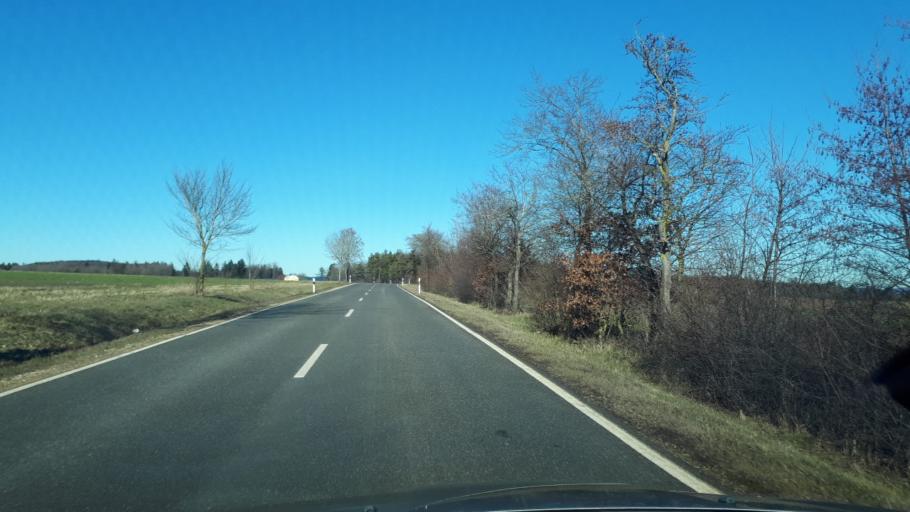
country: DE
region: Rheinland-Pfalz
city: Ellscheid
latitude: 50.1494
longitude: 6.9293
